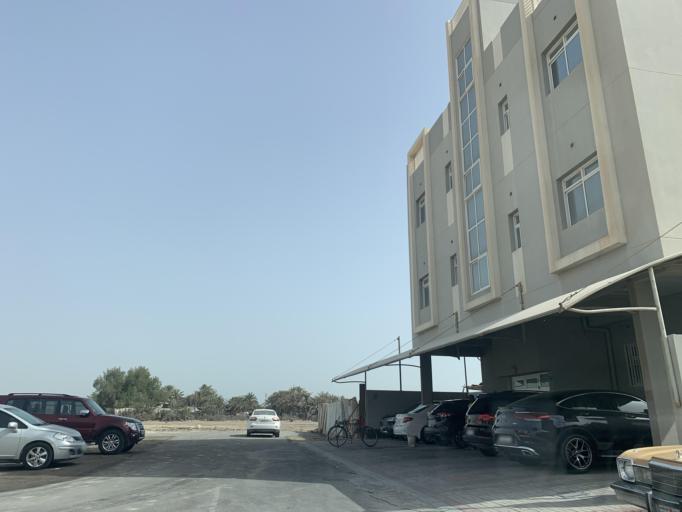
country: BH
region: Northern
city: Sitrah
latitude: 26.1313
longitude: 50.5960
